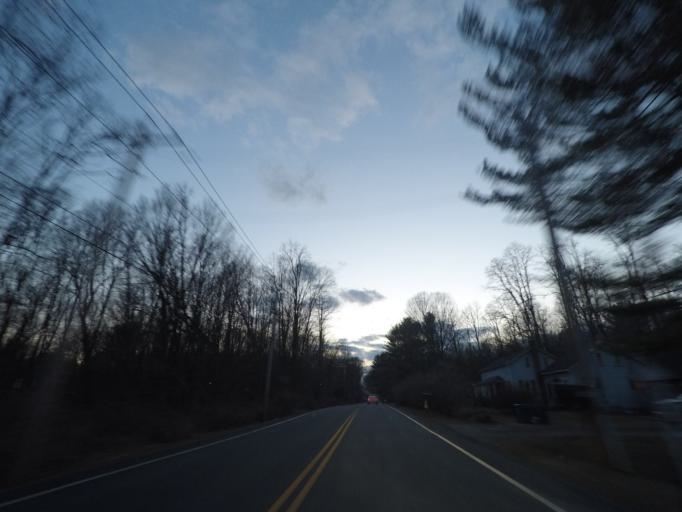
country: US
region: New York
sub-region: Schenectady County
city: Niskayuna
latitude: 42.8323
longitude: -73.8150
